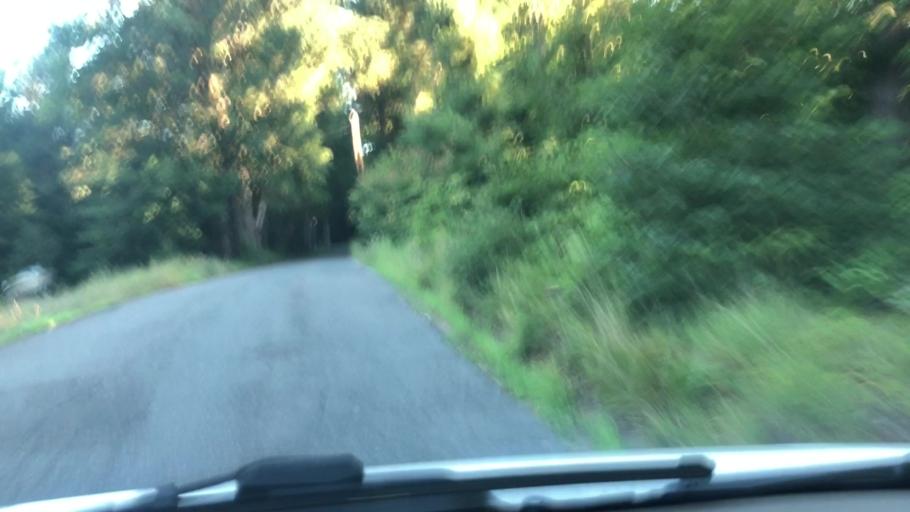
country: US
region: Massachusetts
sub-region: Hampshire County
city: Southampton
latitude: 42.2488
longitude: -72.7145
